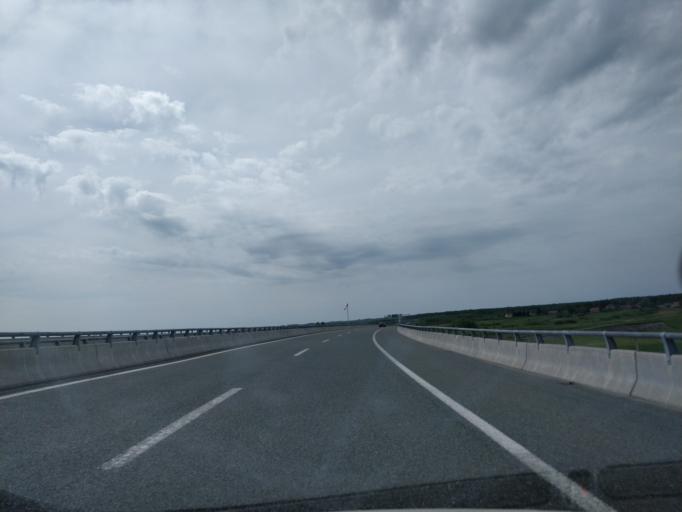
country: HR
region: Zagrebacka
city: Mraclin
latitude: 45.6777
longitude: 16.0803
